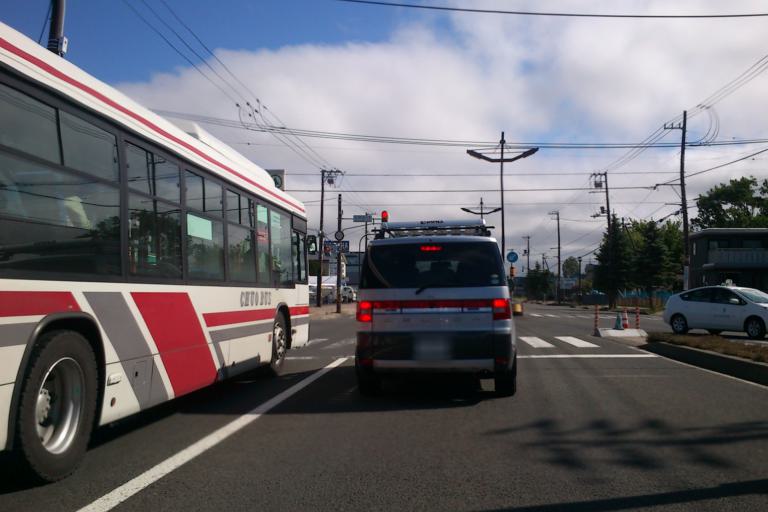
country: JP
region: Hokkaido
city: Ishikari
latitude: 43.1744
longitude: 141.3169
